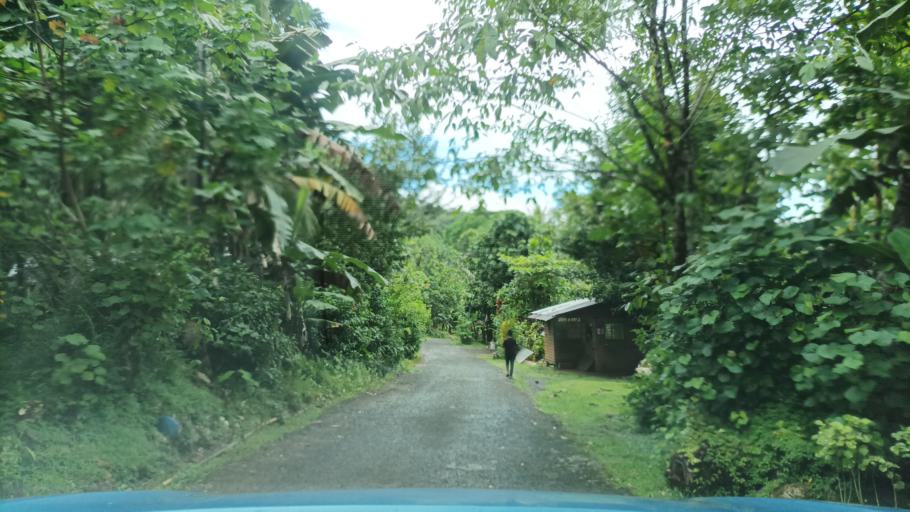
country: FM
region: Pohnpei
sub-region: Sokehs Municipality
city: Palikir - National Government Center
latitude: 6.8349
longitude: 158.1712
